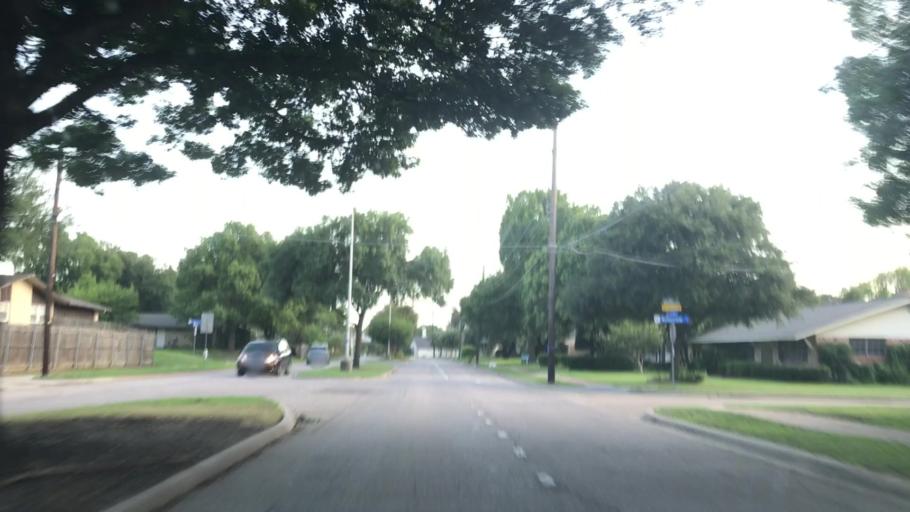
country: US
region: Texas
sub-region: Dallas County
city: Richardson
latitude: 32.9656
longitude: -96.7555
